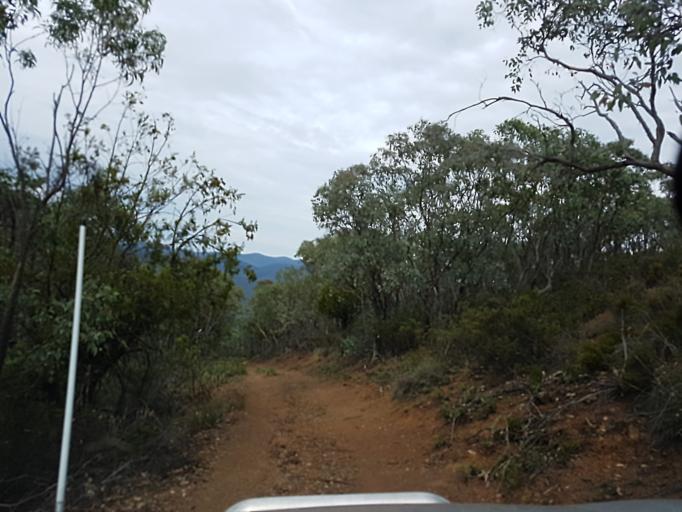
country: AU
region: New South Wales
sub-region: Snowy River
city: Jindabyne
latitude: -36.9955
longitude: 148.4071
